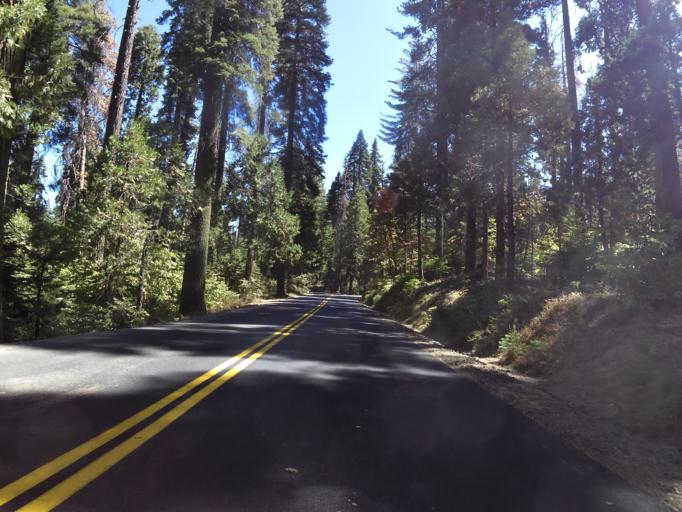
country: US
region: California
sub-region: Madera County
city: Oakhurst
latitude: 37.4121
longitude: -119.5844
